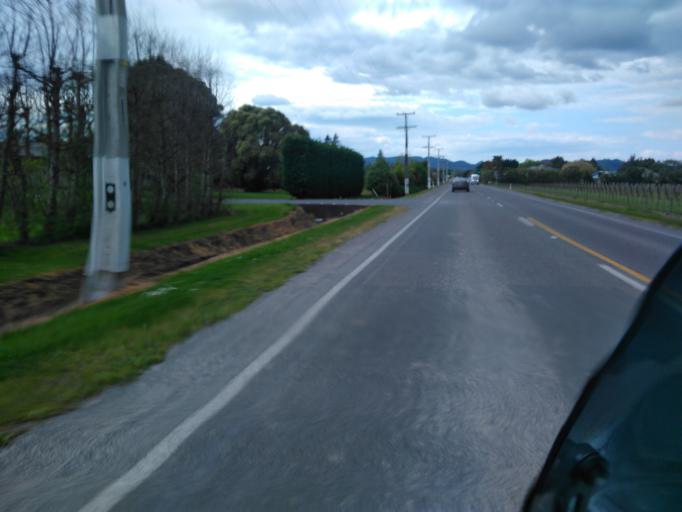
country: NZ
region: Gisborne
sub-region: Gisborne District
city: Gisborne
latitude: -38.6536
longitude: 177.9559
